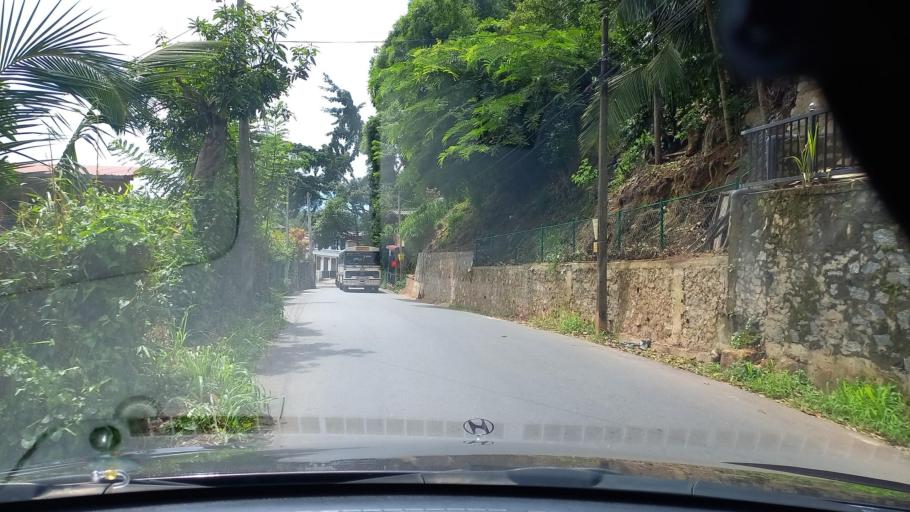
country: LK
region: Central
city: Kandy
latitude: 7.2372
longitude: 80.6022
